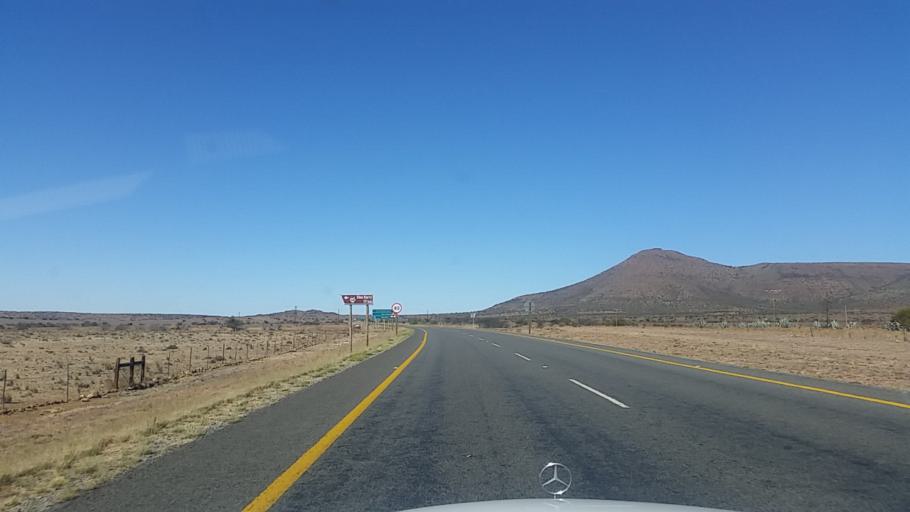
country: ZA
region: Eastern Cape
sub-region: Cacadu District Municipality
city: Graaff-Reinet
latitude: -32.0288
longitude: 24.6284
